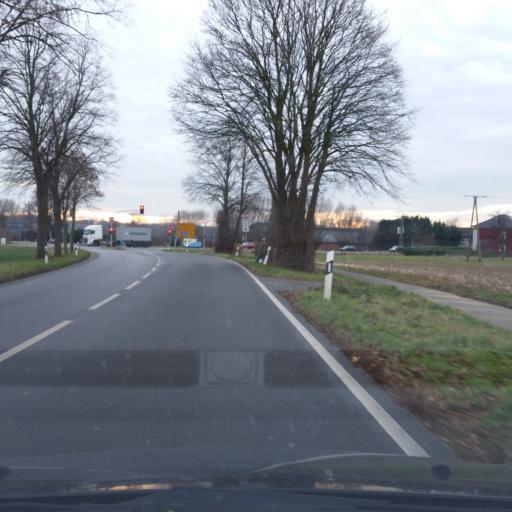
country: DE
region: North Rhine-Westphalia
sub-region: Regierungsbezirk Munster
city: Isselburg
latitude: 51.8126
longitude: 6.5024
